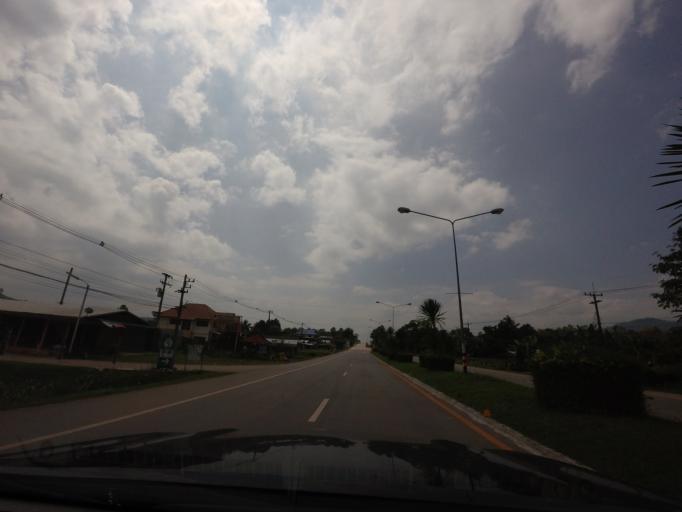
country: TH
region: Loei
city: Phu Ruea
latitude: 17.4486
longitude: 101.3476
